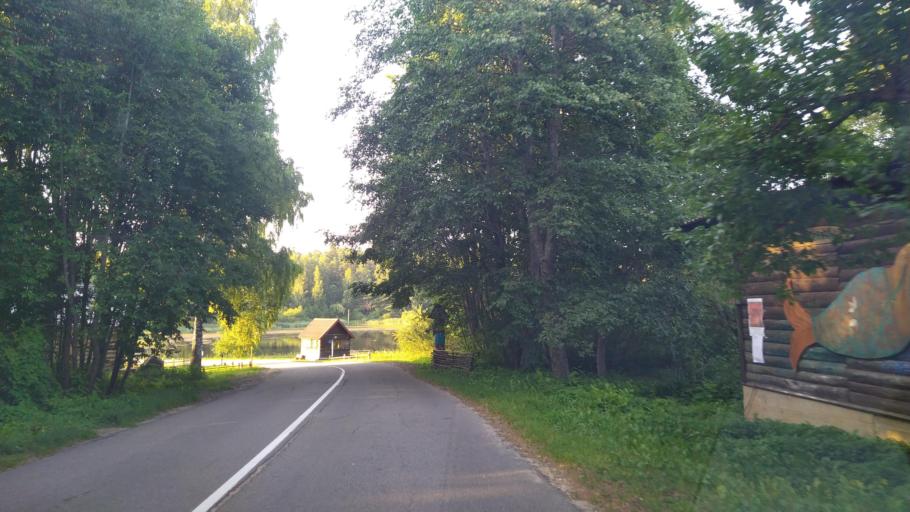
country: RU
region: Pskov
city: Pushkinskiye Gory
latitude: 57.0455
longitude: 28.9178
